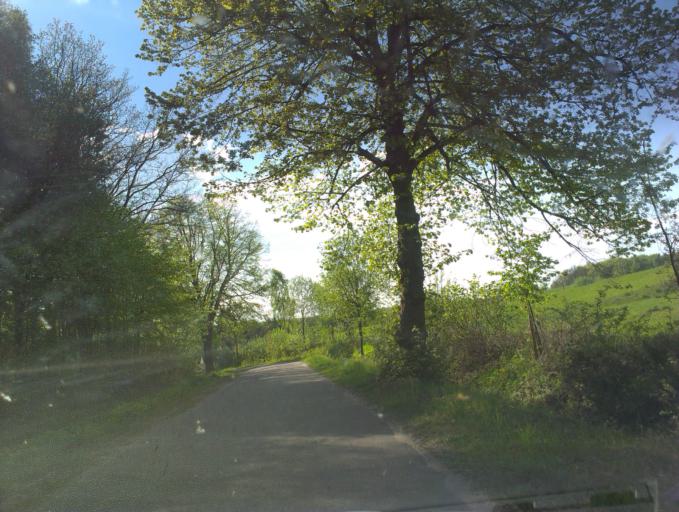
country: PL
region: West Pomeranian Voivodeship
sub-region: Powiat szczecinecki
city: Barwice
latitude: 53.6821
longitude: 16.2719
